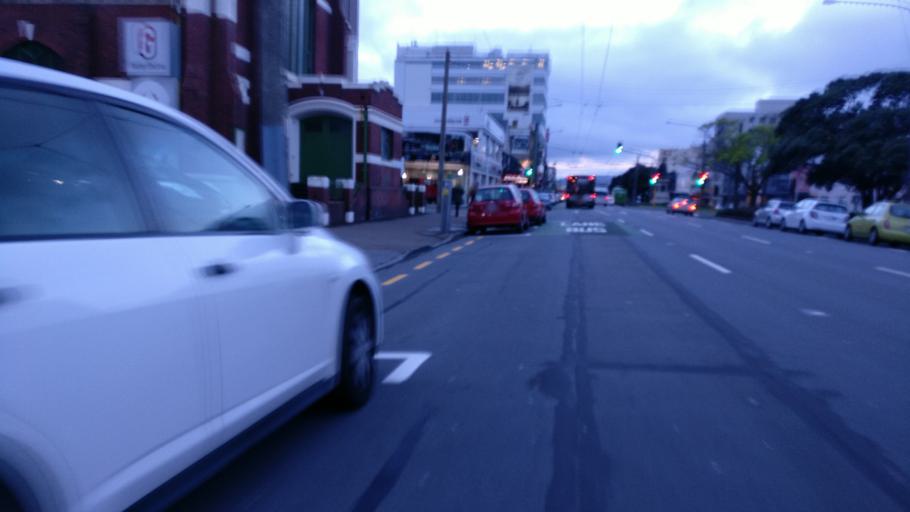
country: NZ
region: Wellington
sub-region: Wellington City
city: Wellington
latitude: -41.2963
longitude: 174.7823
